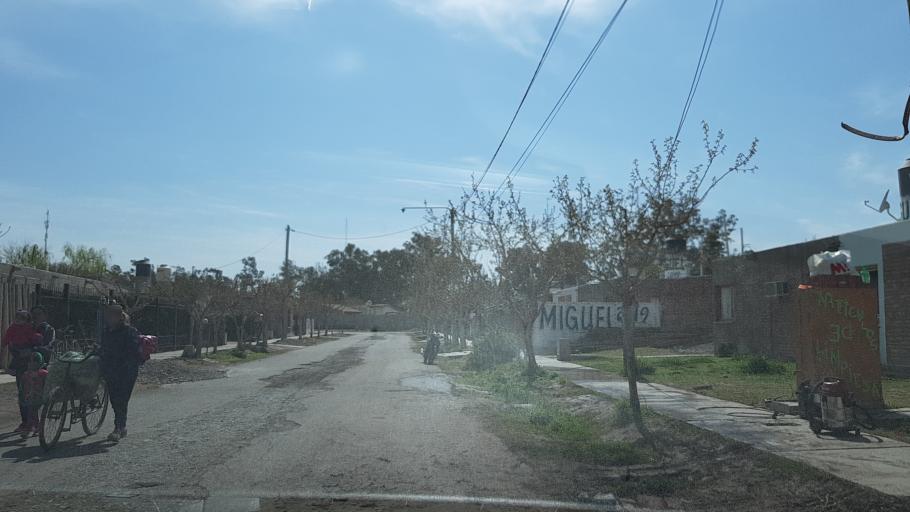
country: AR
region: San Juan
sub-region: Departamento de Zonda
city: Zonda
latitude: -31.5532
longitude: -68.7314
